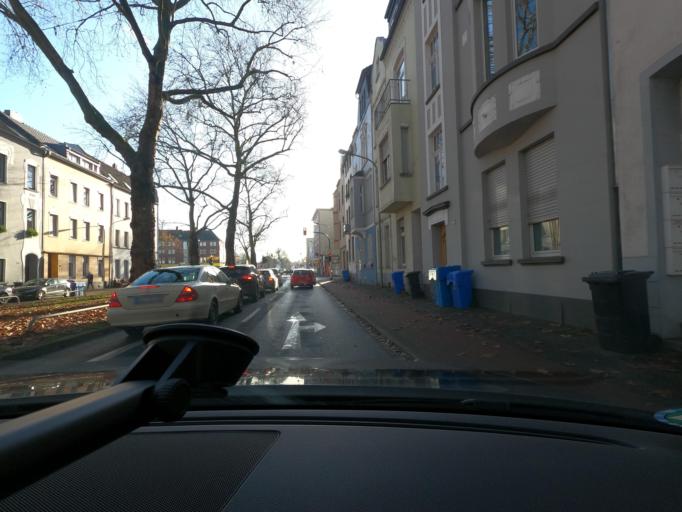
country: DE
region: North Rhine-Westphalia
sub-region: Regierungsbezirk Dusseldorf
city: Krefeld
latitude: 51.3317
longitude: 6.5452
